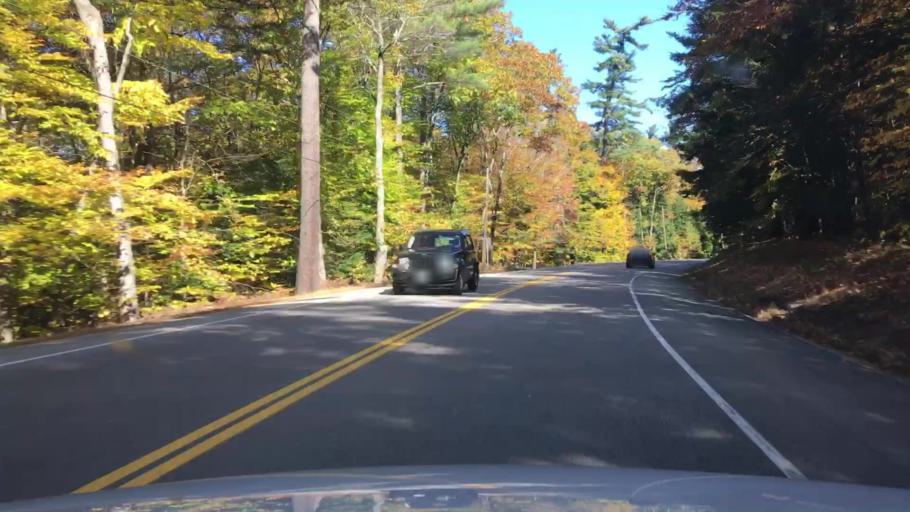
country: US
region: New Hampshire
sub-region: Carroll County
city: Tamworth
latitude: 43.9156
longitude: -71.2373
